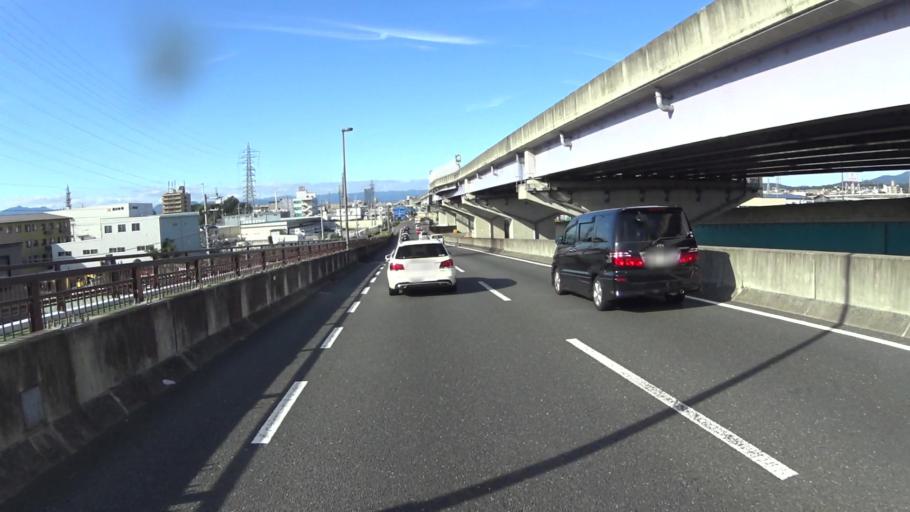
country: JP
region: Kyoto
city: Muko
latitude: 34.9233
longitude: 135.7499
